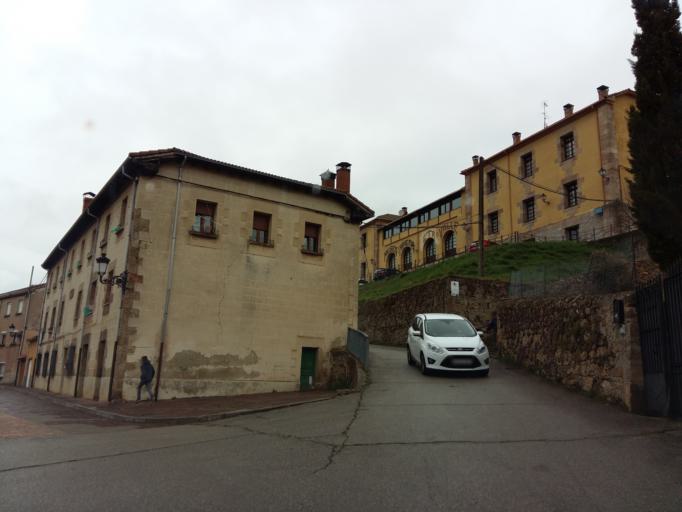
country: ES
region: Castille and Leon
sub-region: Provincia de Palencia
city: Barruelo de Santullan
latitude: 42.9061
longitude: -4.2866
